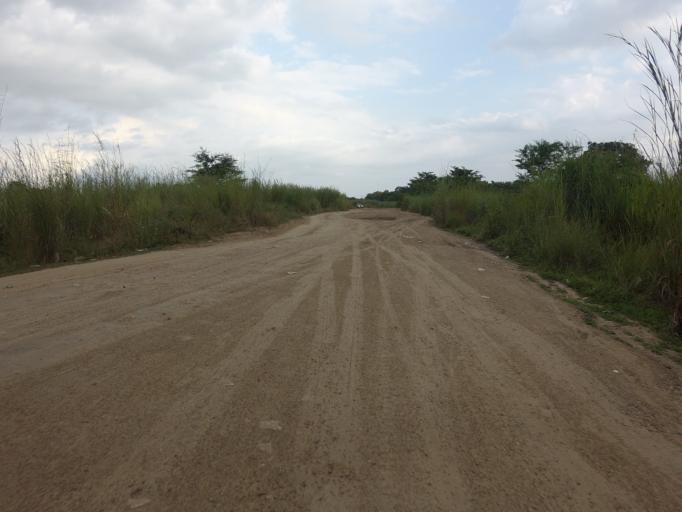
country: GH
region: Volta
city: Ho
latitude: 6.4298
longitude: 0.5083
